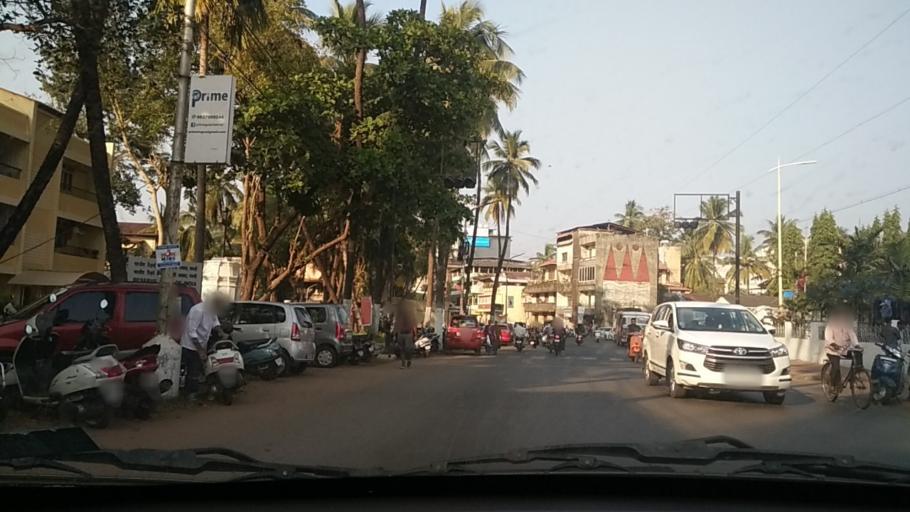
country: IN
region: Goa
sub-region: North Goa
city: Panaji
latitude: 15.4911
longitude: 73.8201
